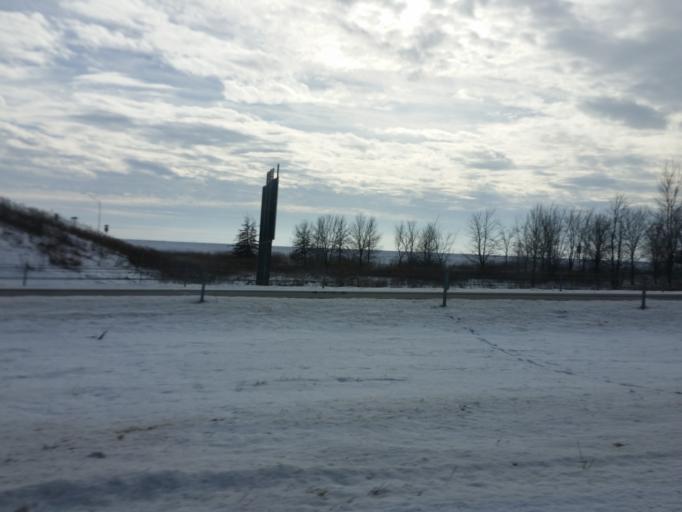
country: US
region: Iowa
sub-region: Buchanan County
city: Independence
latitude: 42.4482
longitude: -91.9197
